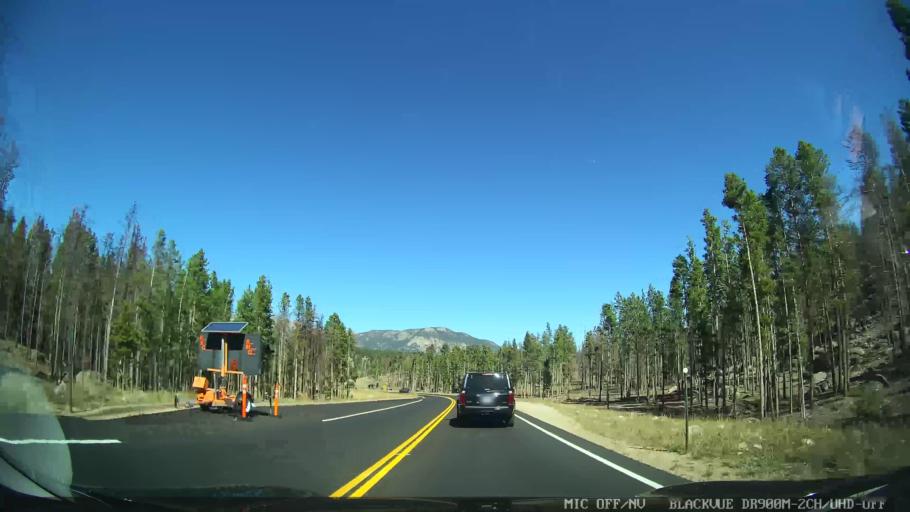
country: US
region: Colorado
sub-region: Larimer County
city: Estes Park
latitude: 40.3366
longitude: -105.6012
